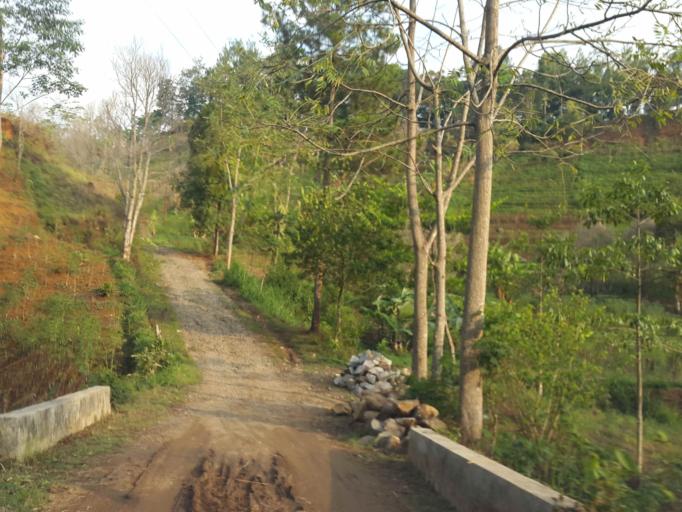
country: ID
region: Central Java
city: Jatiroto
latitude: -7.7053
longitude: 111.1286
